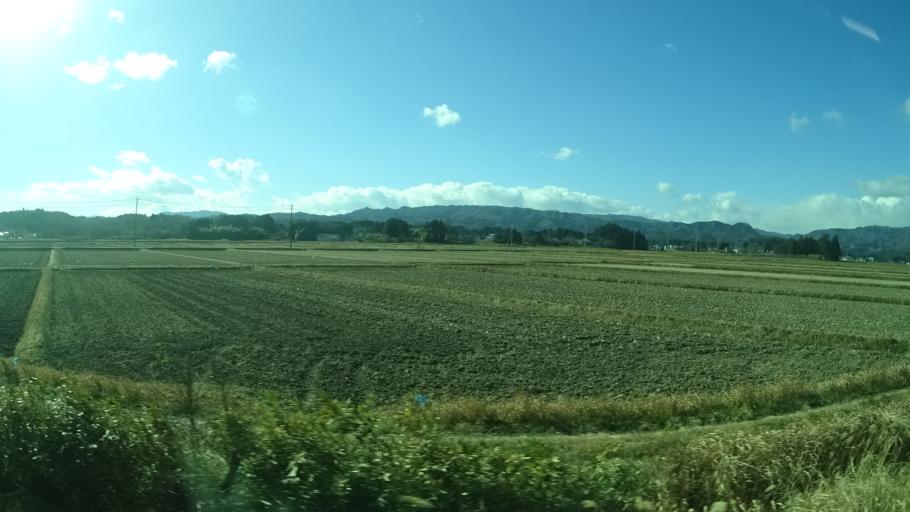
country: JP
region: Miyagi
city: Marumori
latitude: 37.7698
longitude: 140.9225
